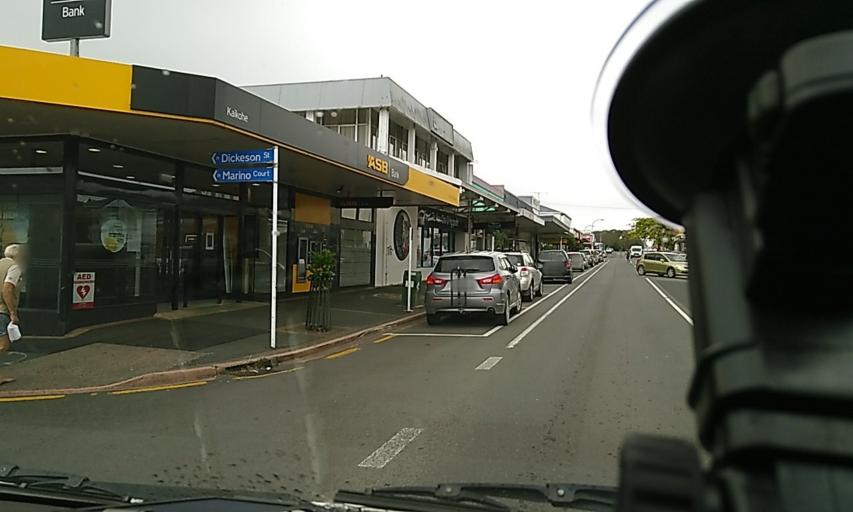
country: NZ
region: Northland
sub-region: Far North District
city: Waimate North
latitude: -35.4078
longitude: 173.7995
